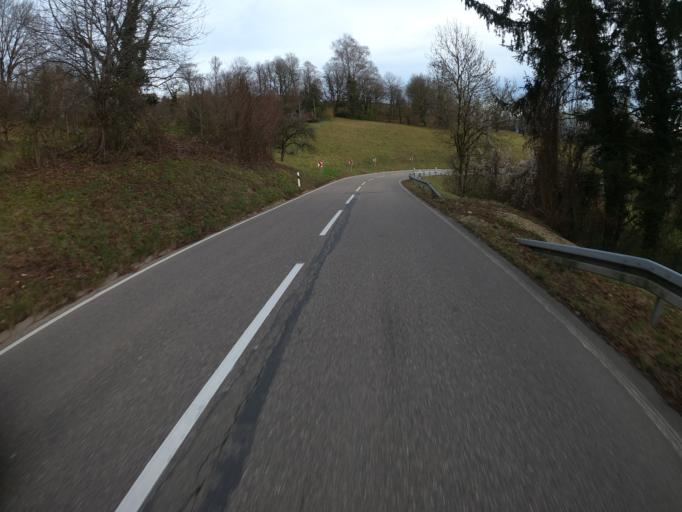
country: DE
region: Baden-Wuerttemberg
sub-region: Regierungsbezirk Stuttgart
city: Ottenbach
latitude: 48.7368
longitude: 9.7176
